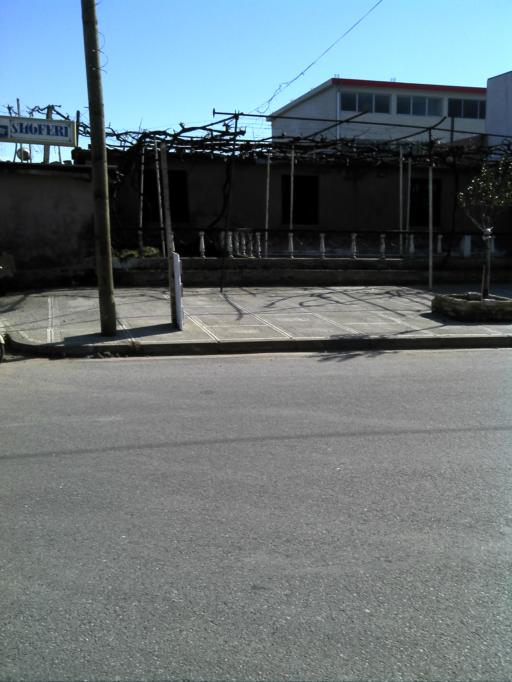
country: AL
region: Shkoder
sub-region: Rrethi i Shkodres
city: Shkoder
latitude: 42.0802
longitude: 19.5285
